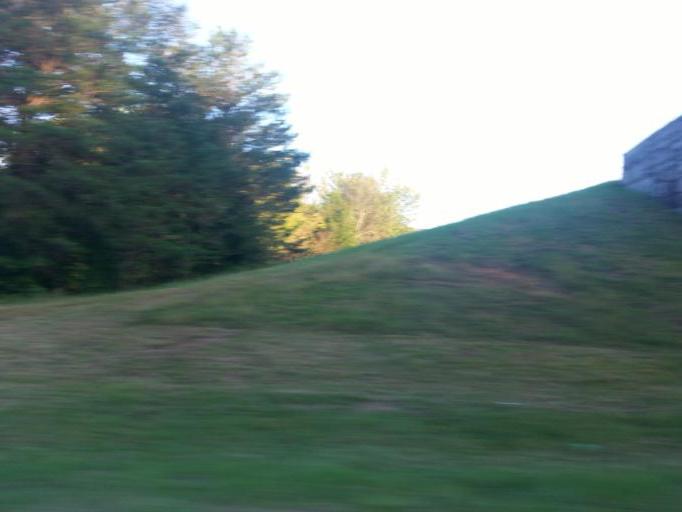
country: US
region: Tennessee
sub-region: Sevier County
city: Pigeon Forge
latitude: 35.7212
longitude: -83.6444
